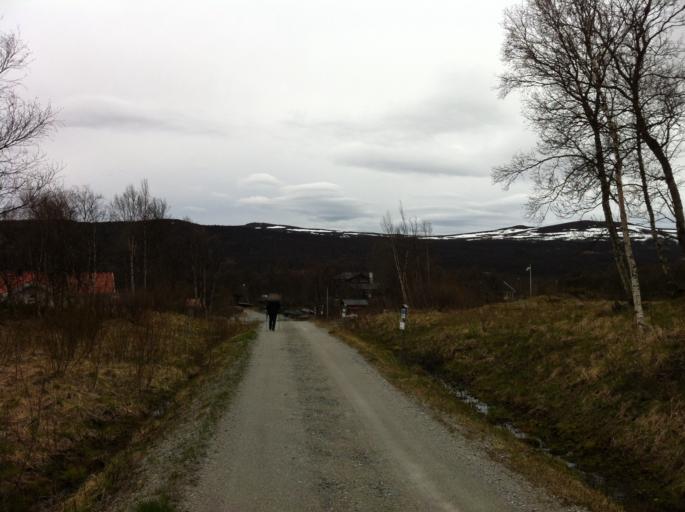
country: NO
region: Sor-Trondelag
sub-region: Tydal
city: Aas
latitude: 62.5509
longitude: 12.3112
